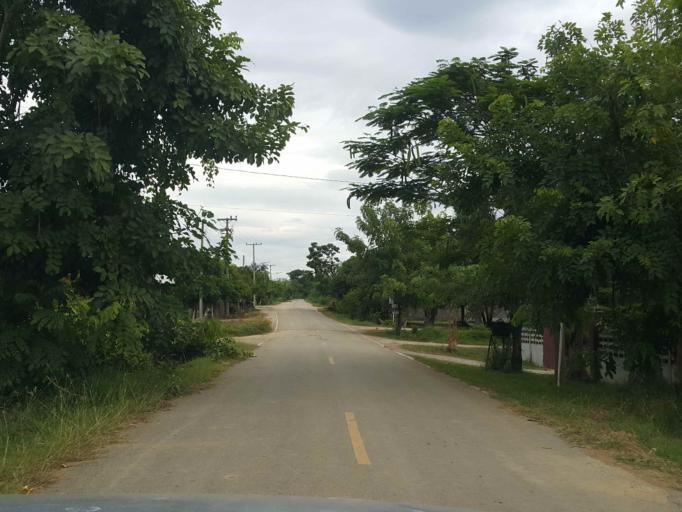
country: TH
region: Sukhothai
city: Thung Saliam
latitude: 17.3429
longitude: 99.4393
